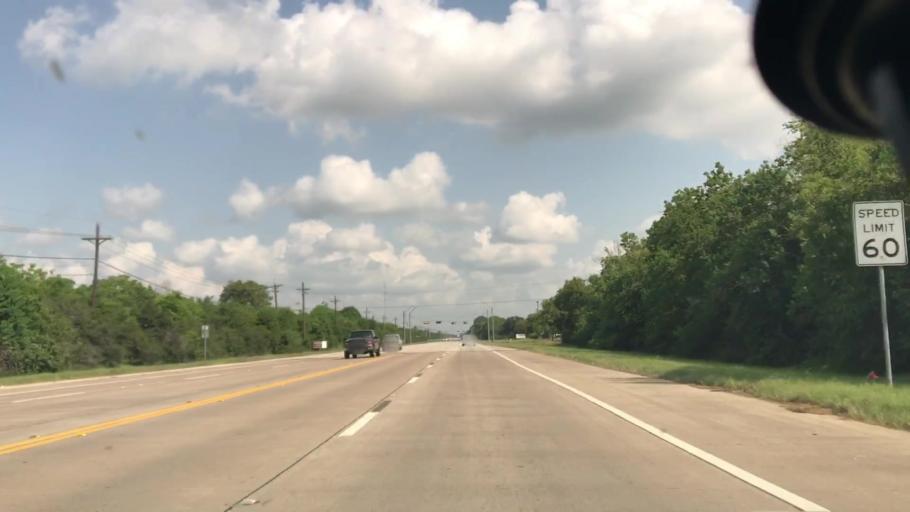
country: US
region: Texas
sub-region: Brazoria County
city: Angleton
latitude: 29.2033
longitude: -95.4351
